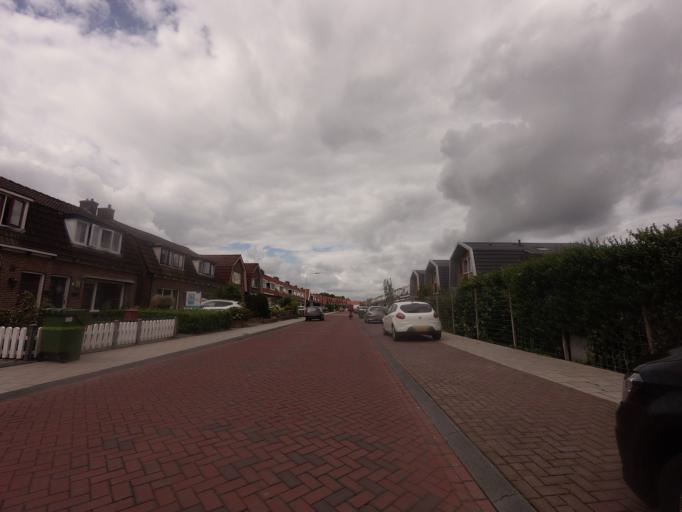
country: NL
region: Drenthe
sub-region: Gemeente Meppel
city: Meppel
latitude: 52.7068
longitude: 6.1807
